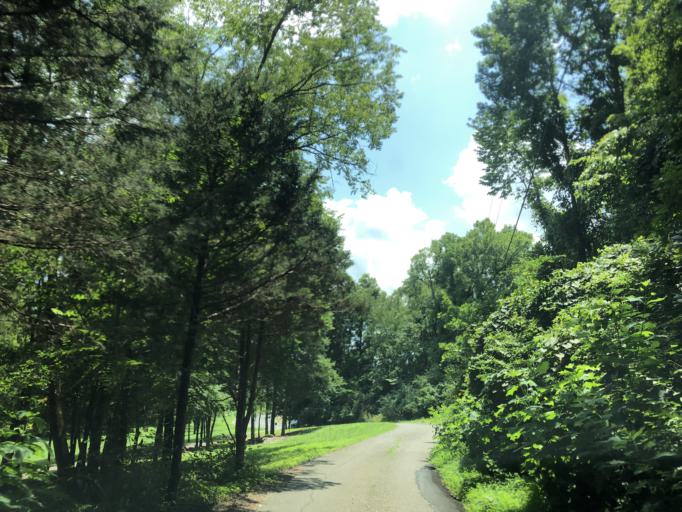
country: US
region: Tennessee
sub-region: Williamson County
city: Brentwood Estates
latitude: 36.0225
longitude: -86.7254
